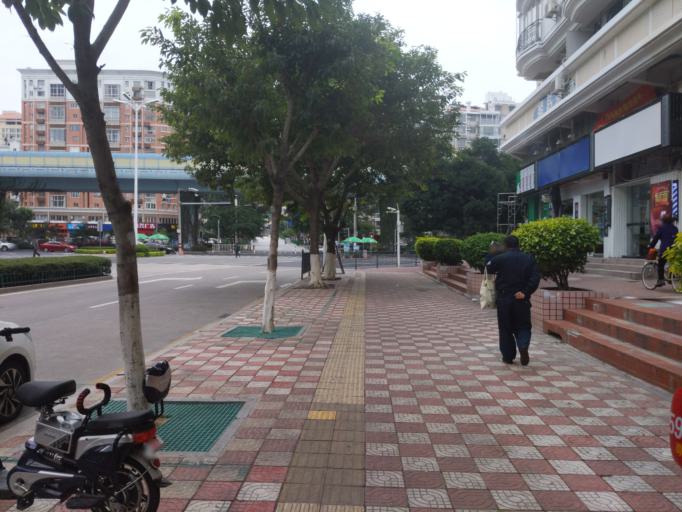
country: CN
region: Fujian
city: Xiamen
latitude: 24.4780
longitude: 118.1609
